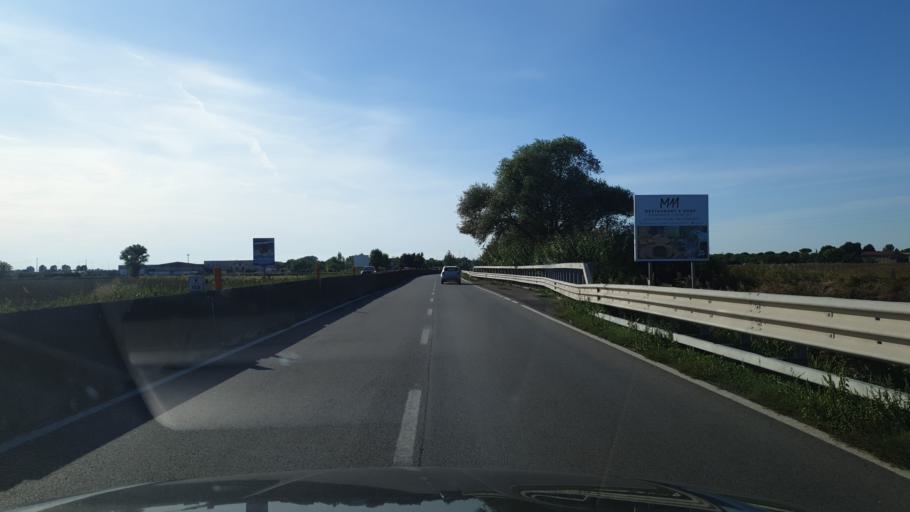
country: IT
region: Emilia-Romagna
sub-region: Provincia di Ravenna
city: Classe
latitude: 44.3765
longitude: 12.2202
